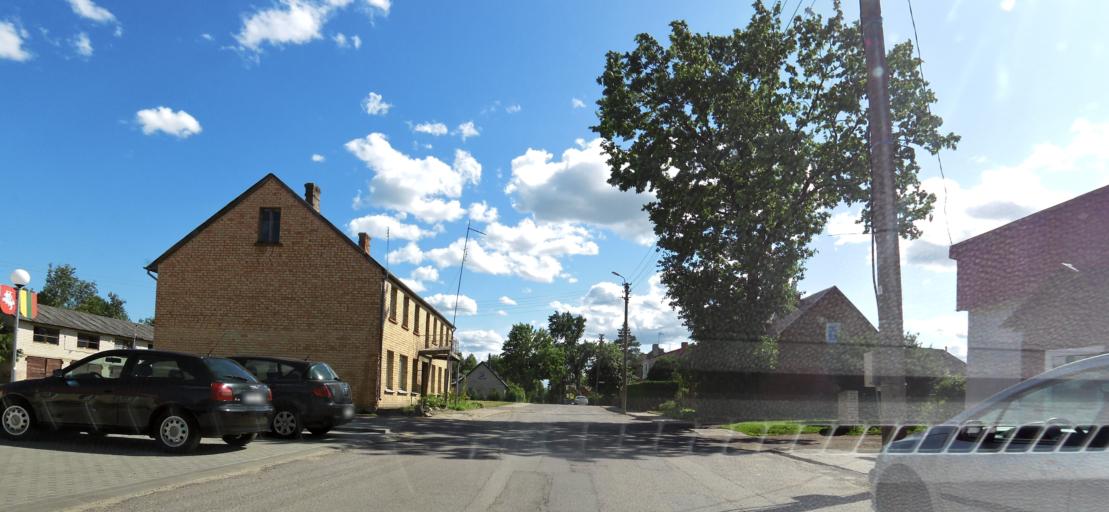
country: LT
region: Panevezys
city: Pasvalys
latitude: 56.1679
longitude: 24.2108
